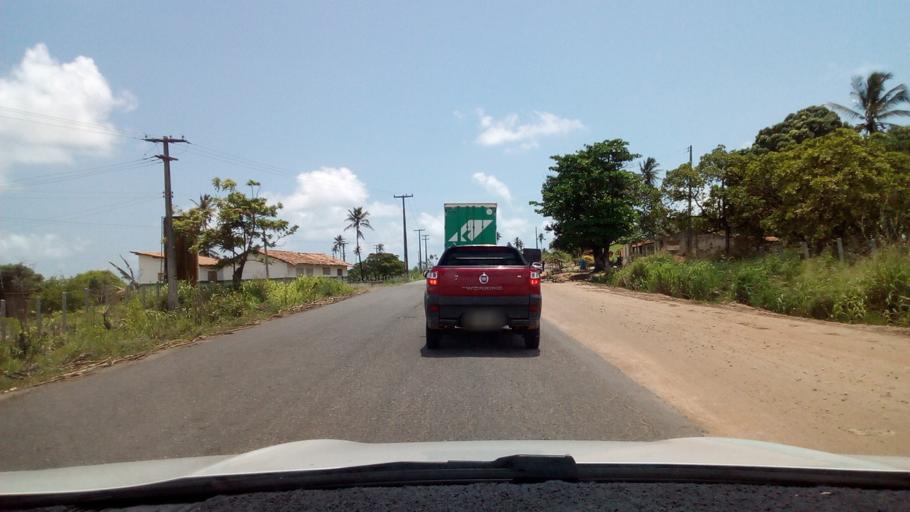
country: BR
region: Paraiba
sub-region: Caapora
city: Caapora
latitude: -7.5170
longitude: -34.8682
